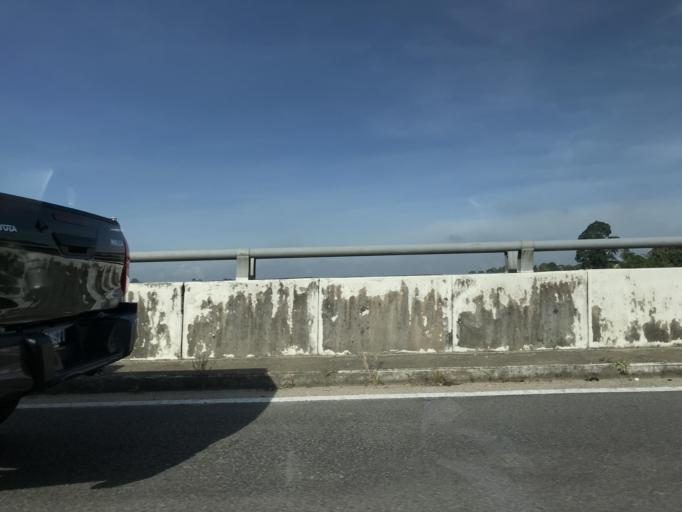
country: MY
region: Kelantan
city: Kampong Kadok
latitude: 6.0583
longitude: 102.2116
